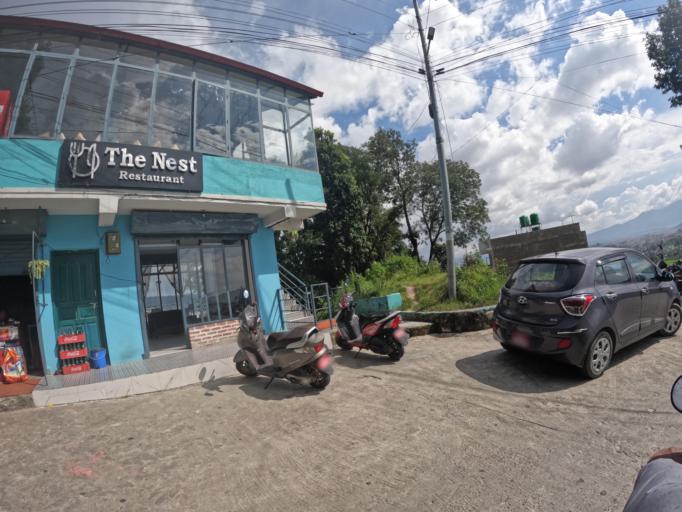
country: NP
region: Central Region
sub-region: Bagmati Zone
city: Kathmandu
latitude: 27.7758
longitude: 85.3410
